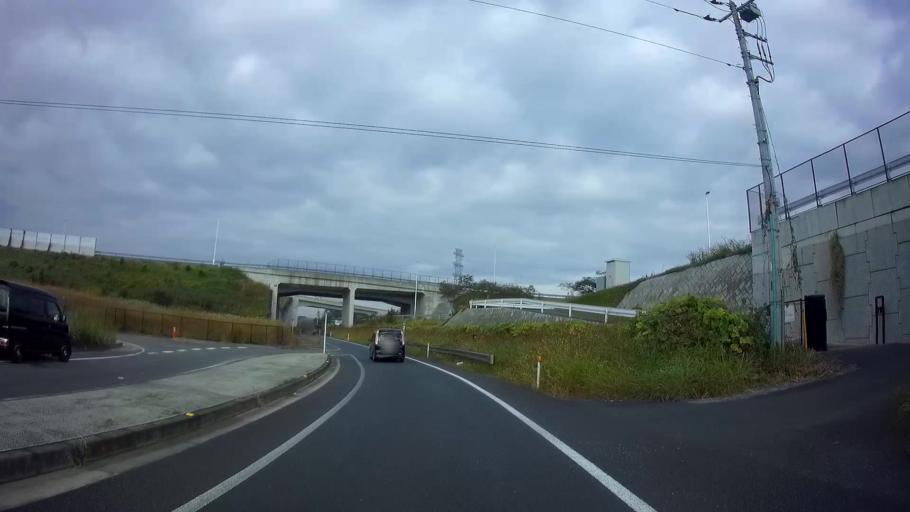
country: JP
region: Saitama
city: Okegawa
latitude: 36.0003
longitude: 139.5198
